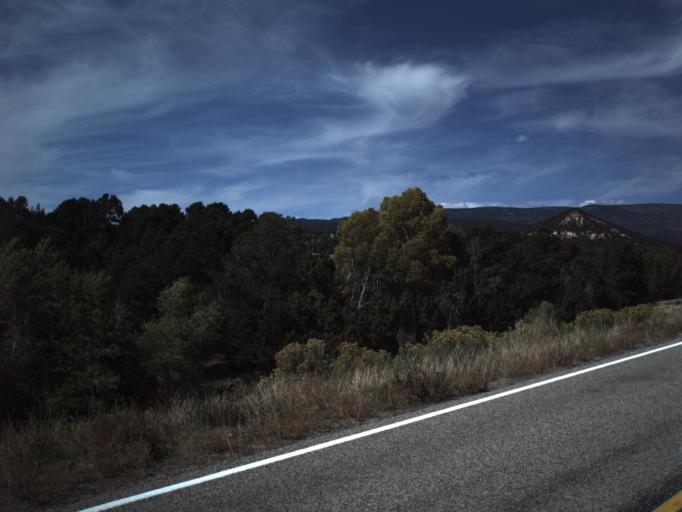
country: US
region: Utah
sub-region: Wayne County
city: Loa
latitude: 37.9328
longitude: -111.4306
